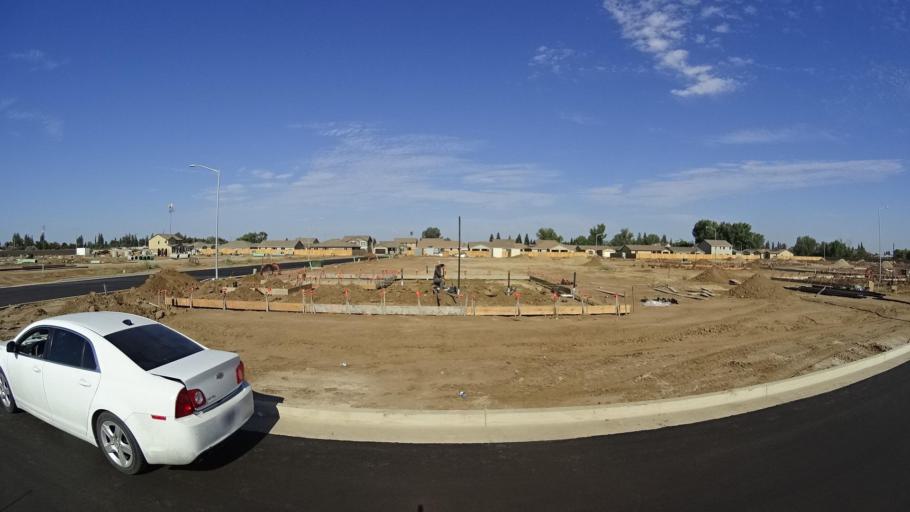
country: US
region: California
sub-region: Fresno County
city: Sunnyside
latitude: 36.7660
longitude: -119.6592
